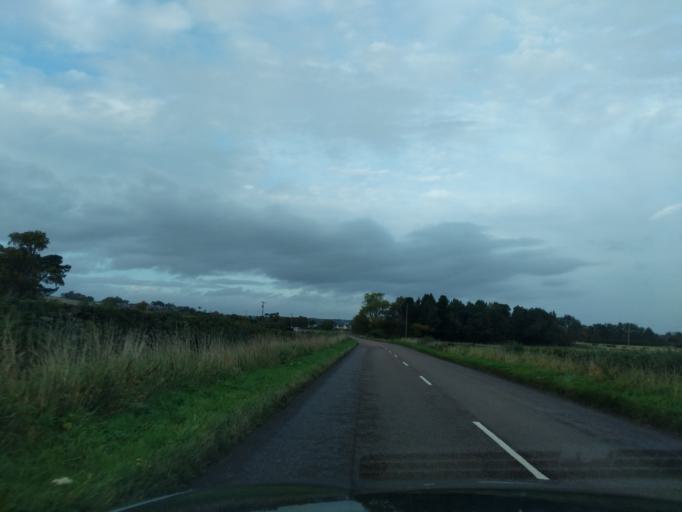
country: GB
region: Scotland
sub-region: Fife
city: Tayport
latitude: 56.4344
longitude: -2.8845
